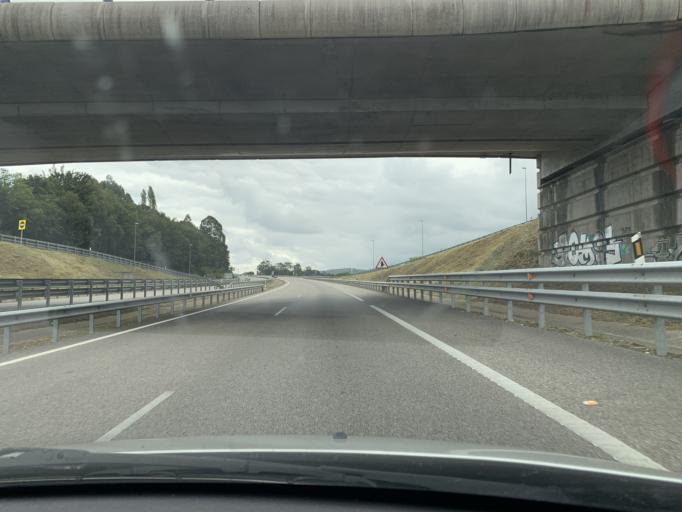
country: ES
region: Asturias
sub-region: Province of Asturias
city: Llanes
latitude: 43.4051
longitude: -4.7603
